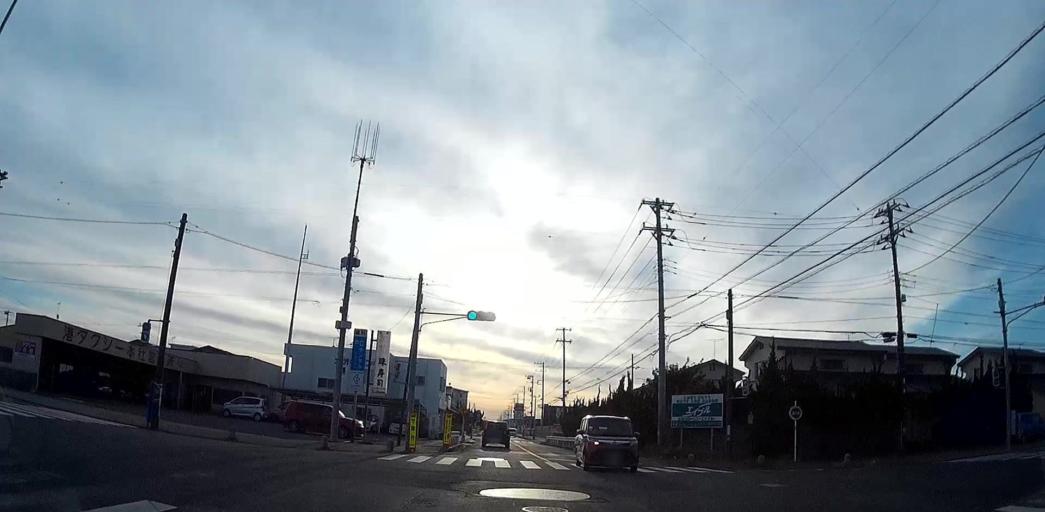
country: JP
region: Chiba
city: Hasaki
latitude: 35.7937
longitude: 140.7729
